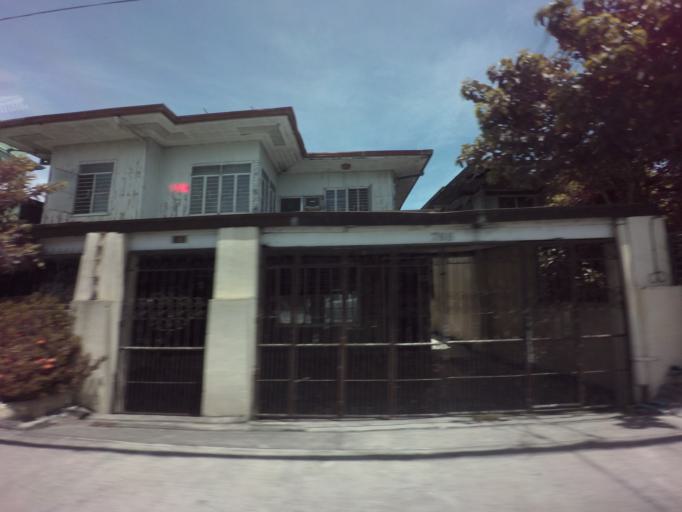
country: PH
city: Sambayanihan People's Village
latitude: 14.4621
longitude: 121.0547
